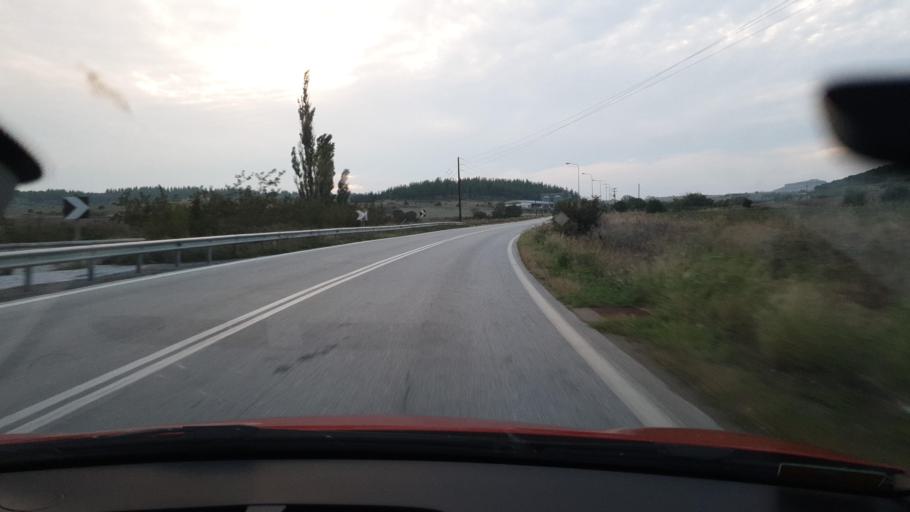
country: GR
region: Central Macedonia
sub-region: Nomos Kilkis
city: Kristoni
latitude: 40.9953
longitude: 22.7426
